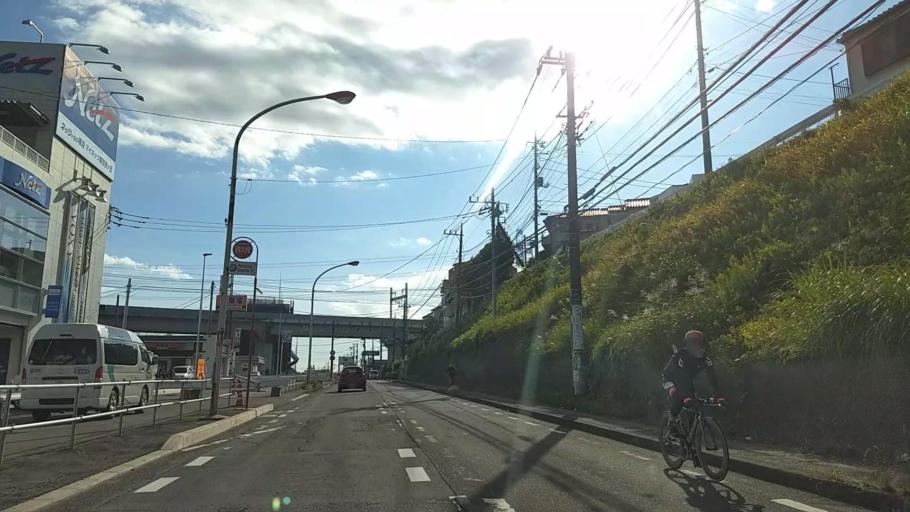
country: JP
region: Tokyo
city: Chofugaoka
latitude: 35.6005
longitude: 139.5003
